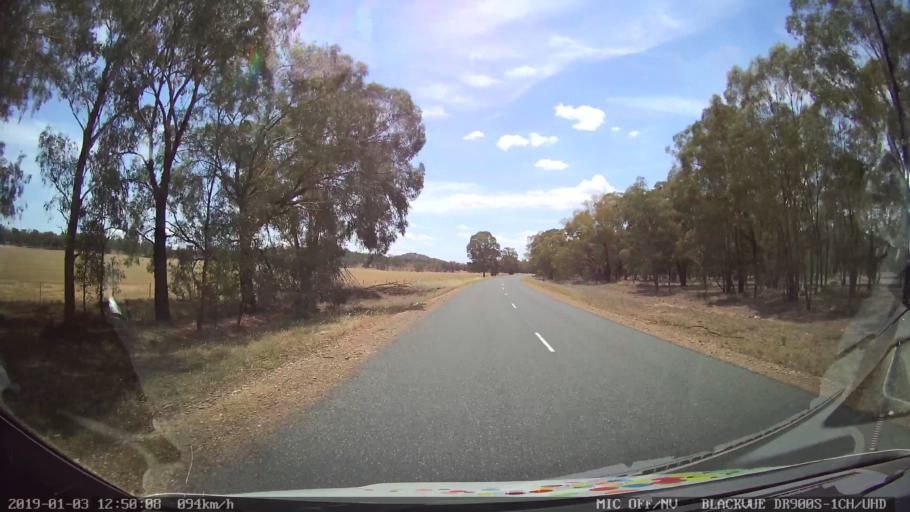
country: AU
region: New South Wales
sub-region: Weddin
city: Grenfell
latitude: -33.6948
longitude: 148.2667
